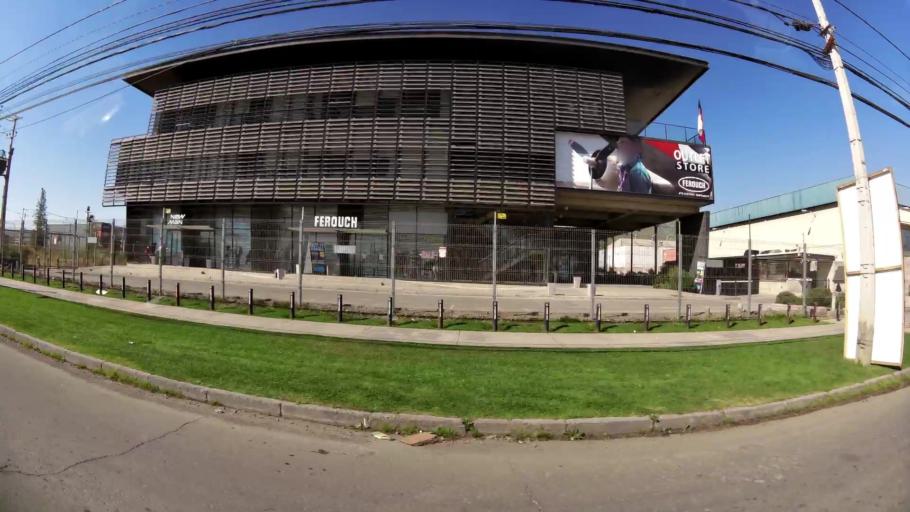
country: CL
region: Santiago Metropolitan
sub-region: Provincia de Chacabuco
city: Chicureo Abajo
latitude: -33.3299
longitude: -70.7122
